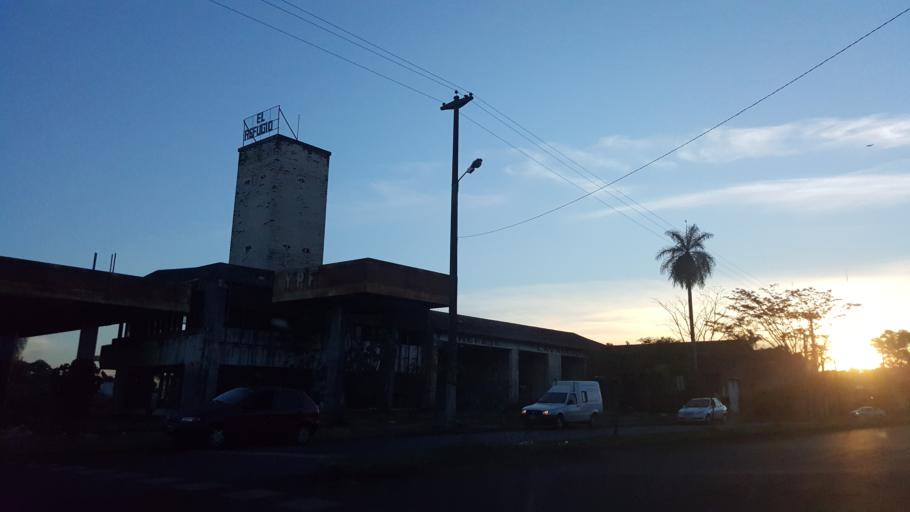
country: AR
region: Misiones
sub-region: Departamento de Capital
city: Posadas
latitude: -27.3975
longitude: -55.9019
